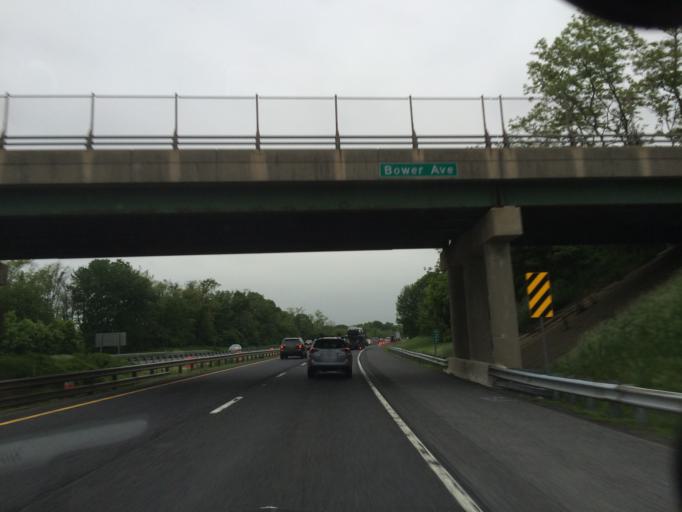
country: US
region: Maryland
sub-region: Washington County
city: Halfway
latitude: 39.6068
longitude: -77.7737
